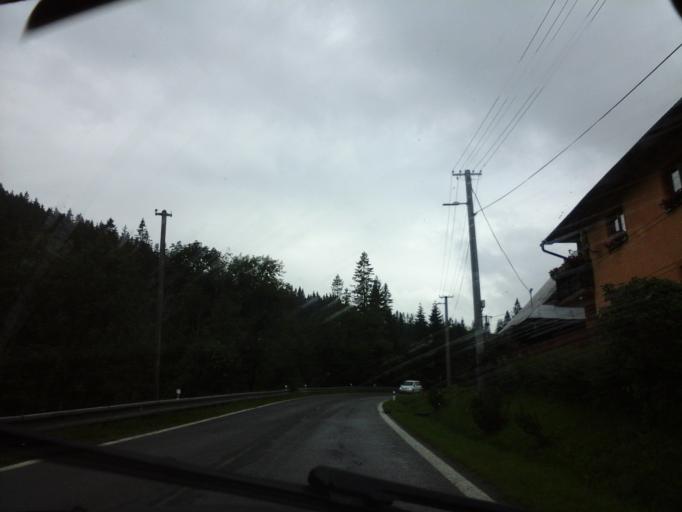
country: SK
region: Presovsky
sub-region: Okres Poprad
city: Zdiar
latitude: 49.2667
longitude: 20.2874
